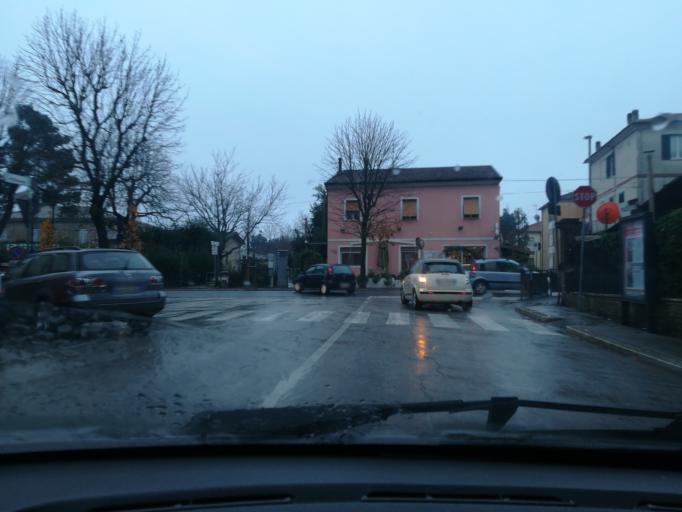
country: IT
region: The Marches
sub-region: Provincia di Macerata
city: Macerata
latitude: 43.2982
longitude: 13.4302
